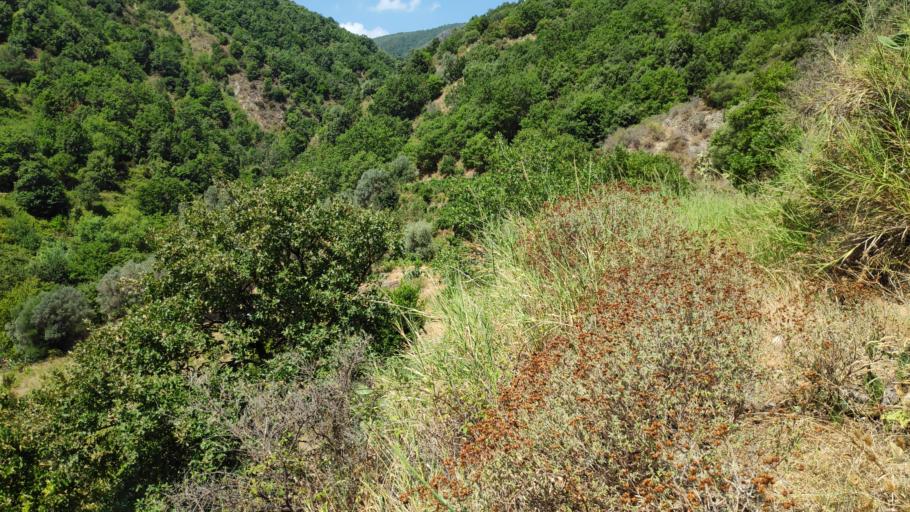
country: IT
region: Calabria
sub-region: Provincia di Reggio Calabria
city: Bivongi
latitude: 38.4943
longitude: 16.4395
